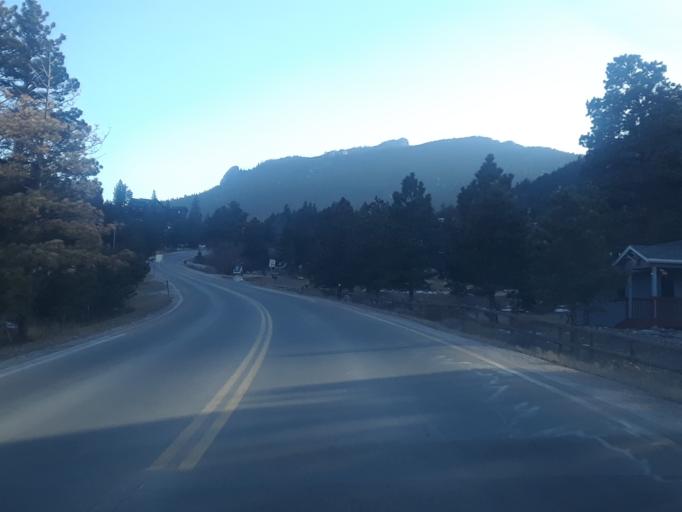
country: US
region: Colorado
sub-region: Larimer County
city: Estes Park
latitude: 40.3560
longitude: -105.5420
